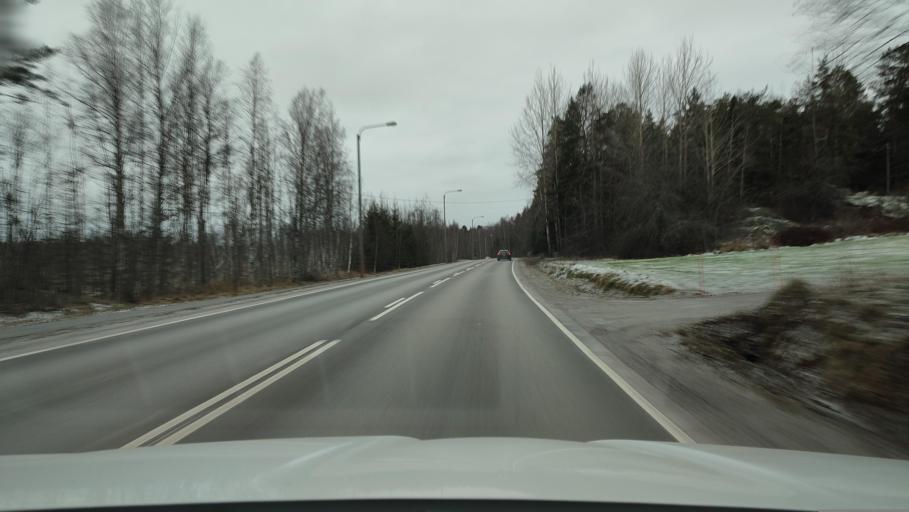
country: FI
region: Ostrobothnia
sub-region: Vaasa
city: Smedsby
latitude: 63.1406
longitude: 21.7021
